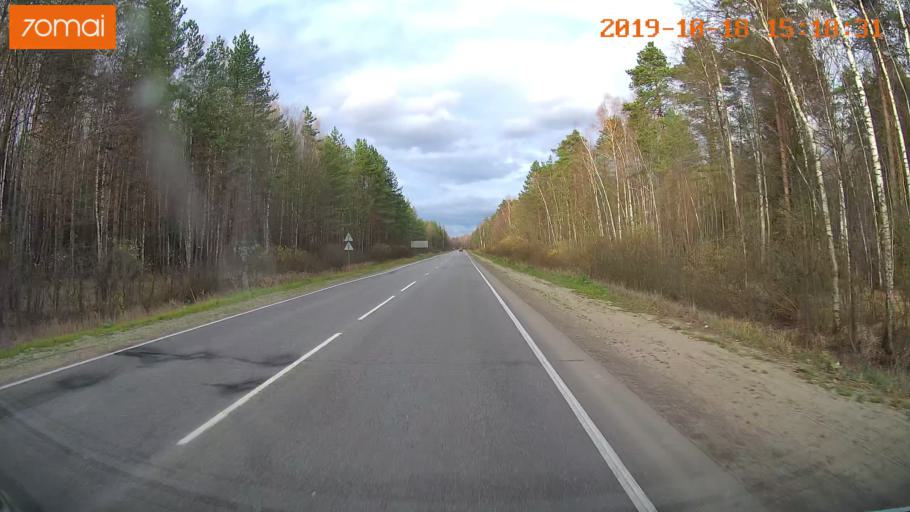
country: RU
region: Vladimir
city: Anopino
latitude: 55.6603
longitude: 40.7295
